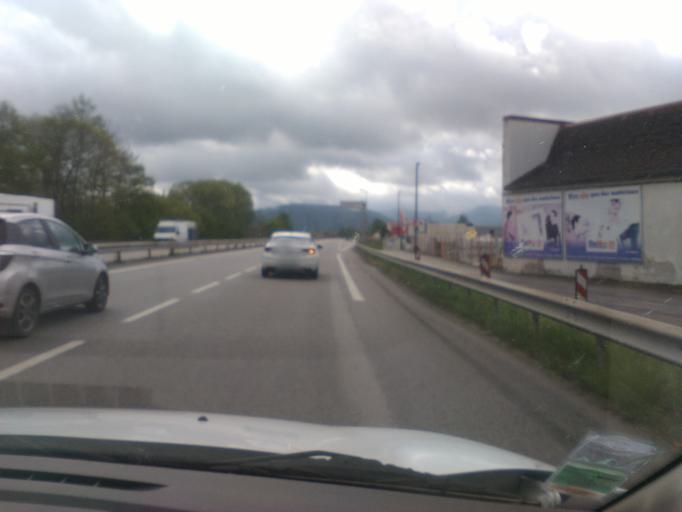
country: FR
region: Lorraine
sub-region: Departement des Vosges
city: Remiremont
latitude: 48.0257
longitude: 6.5887
